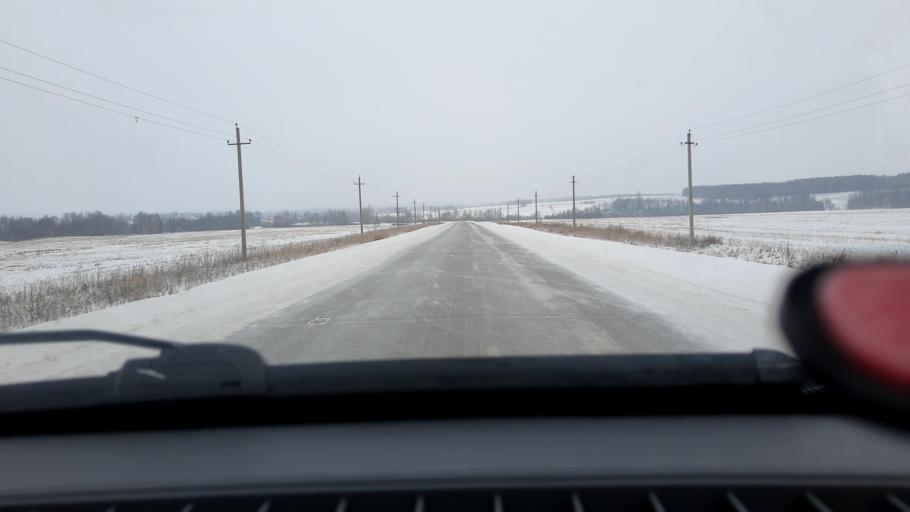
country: RU
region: Bashkortostan
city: Iglino
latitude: 54.6942
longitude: 56.4159
